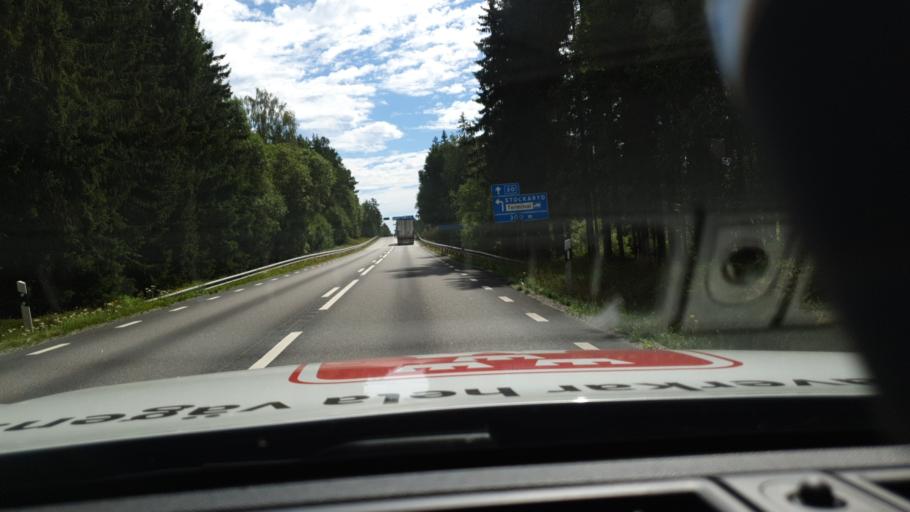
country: SE
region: Joenkoeping
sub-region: Savsjo Kommun
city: Vrigstad
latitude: 57.3142
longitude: 14.5019
